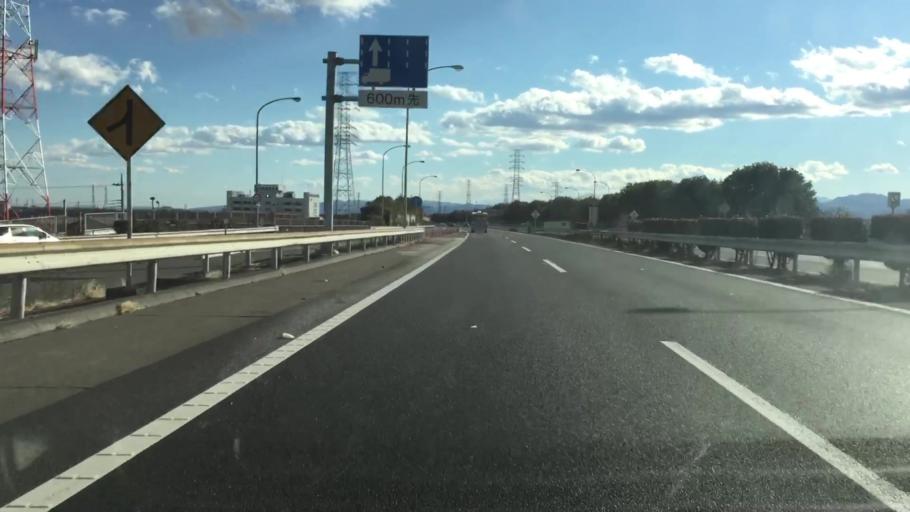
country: JP
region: Gunma
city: Maebashi-shi
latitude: 36.3744
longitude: 139.0281
